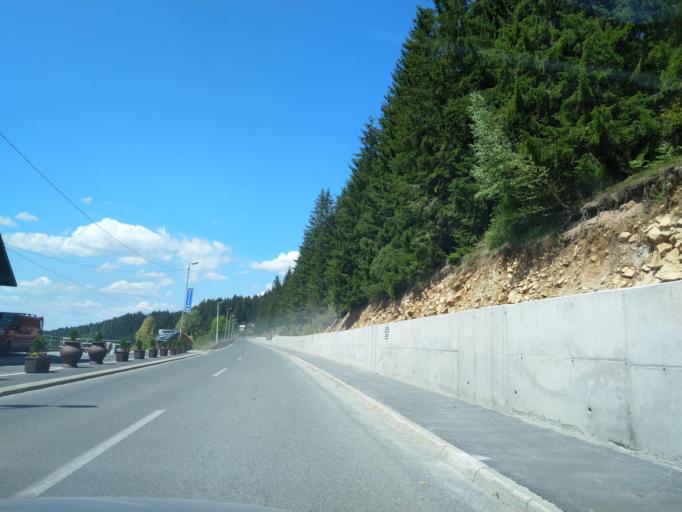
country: RS
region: Central Serbia
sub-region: Zlatiborski Okrug
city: Nova Varos
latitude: 43.4389
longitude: 19.8223
